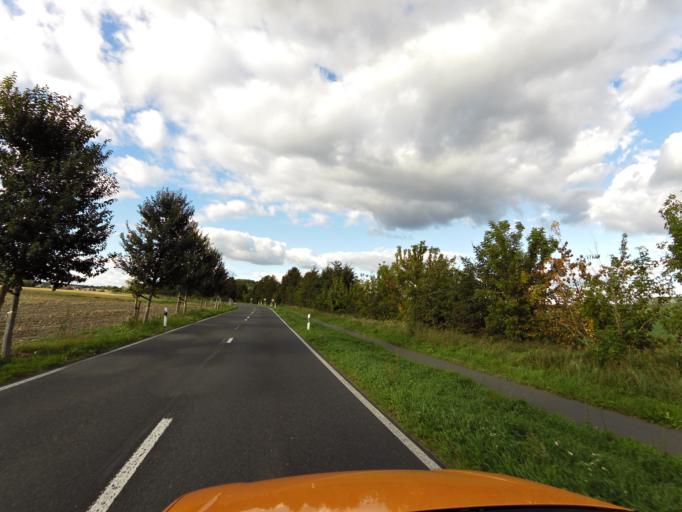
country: DE
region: Brandenburg
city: Trebbin
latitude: 52.1779
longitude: 13.1760
